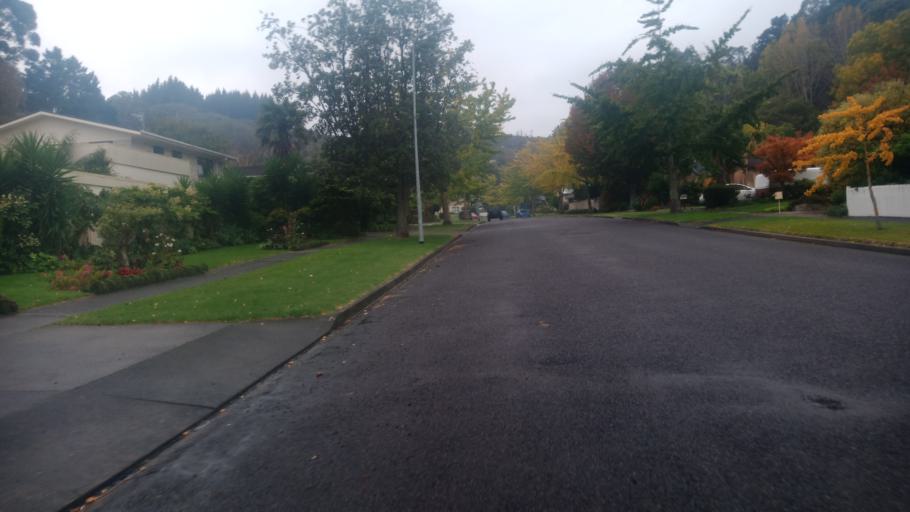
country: NZ
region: Gisborne
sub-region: Gisborne District
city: Gisborne
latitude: -38.6546
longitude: 178.0396
